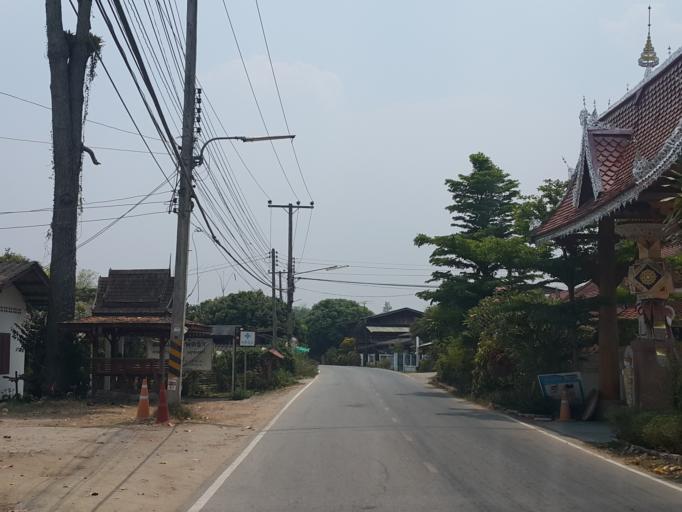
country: TH
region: Chiang Mai
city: Mae Taeng
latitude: 19.0446
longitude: 98.8677
